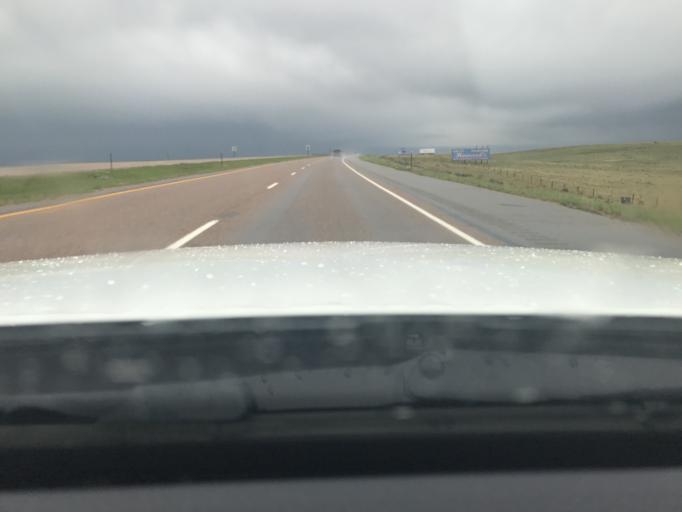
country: US
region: Wyoming
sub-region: Converse County
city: Douglas
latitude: 42.7373
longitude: -105.3542
